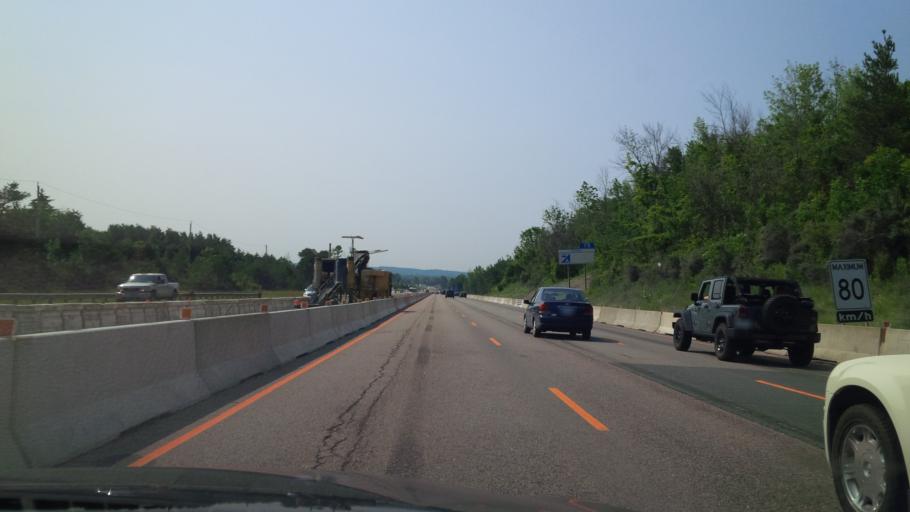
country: CA
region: Ontario
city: Innisfil
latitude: 44.2234
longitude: -79.6633
